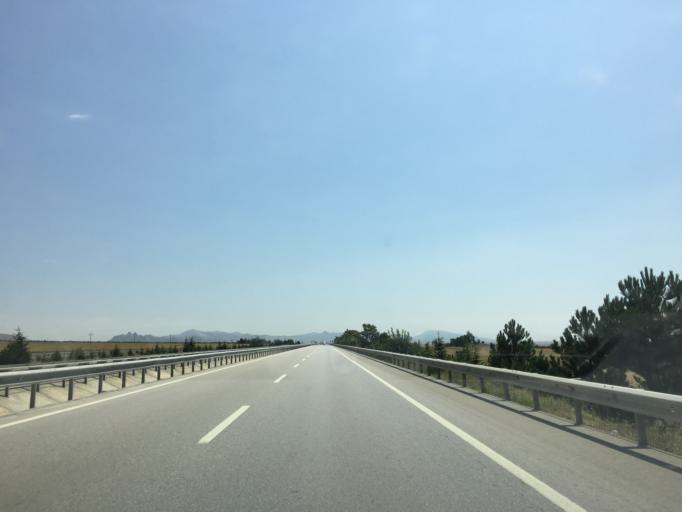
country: TR
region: Eskisehir
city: Sivrihisar
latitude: 39.4598
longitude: 31.3835
